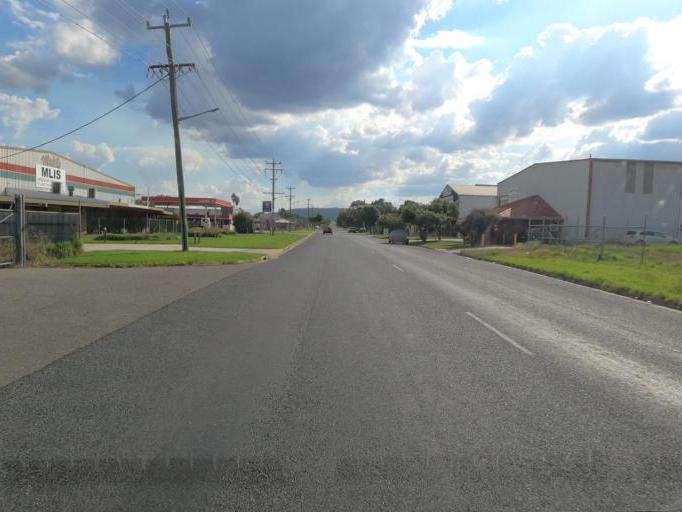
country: AU
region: New South Wales
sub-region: Albury Municipality
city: East Albury
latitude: -36.0703
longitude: 146.9412
